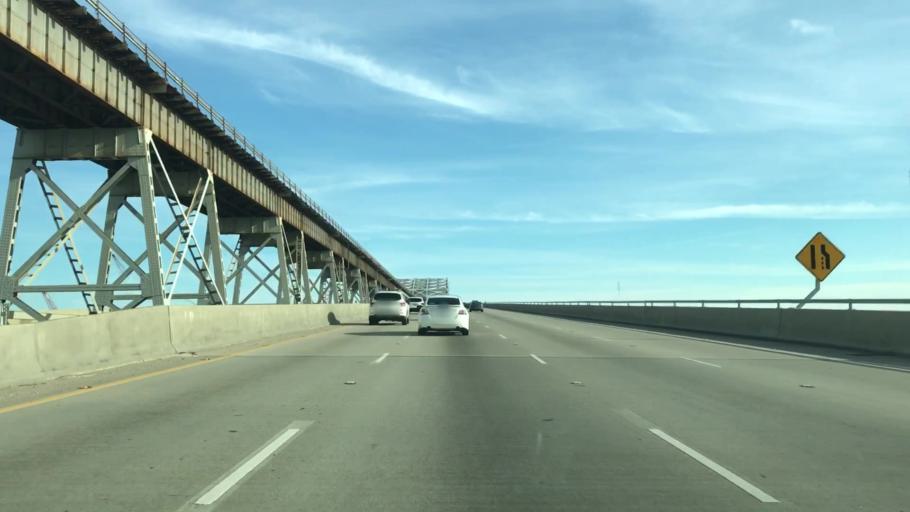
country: US
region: Louisiana
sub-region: Jefferson Parish
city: Elmwood
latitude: 29.9501
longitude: -90.1755
